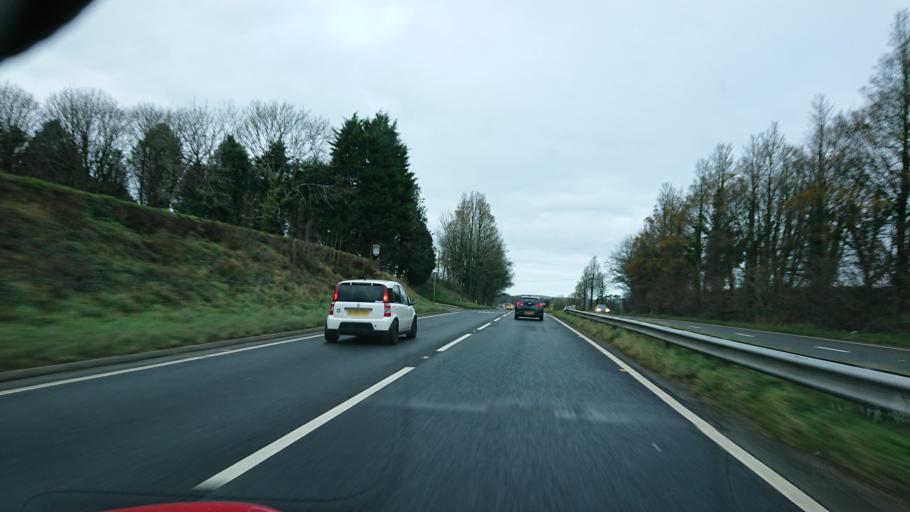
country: GB
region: England
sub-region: Cornwall
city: Liskeard
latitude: 50.4418
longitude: -4.4443
